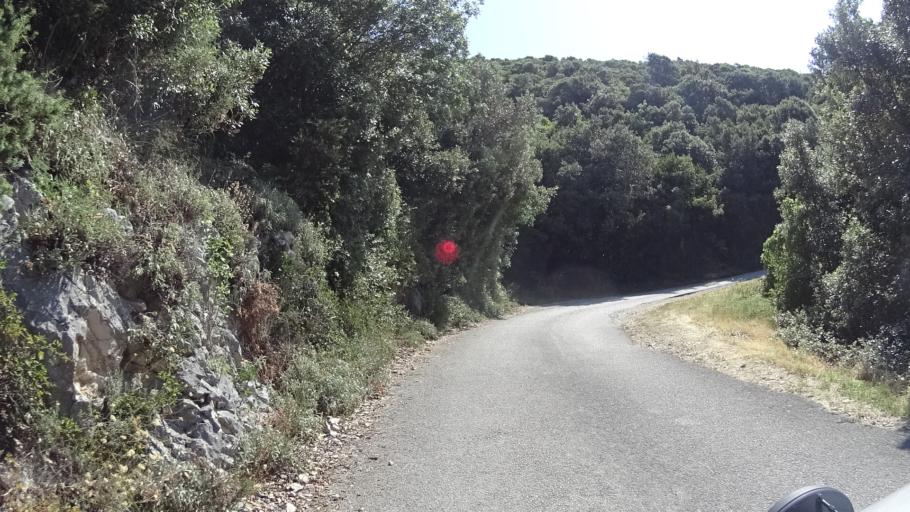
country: HR
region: Istarska
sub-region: Grad Labin
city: Rabac
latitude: 44.9752
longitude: 14.1390
